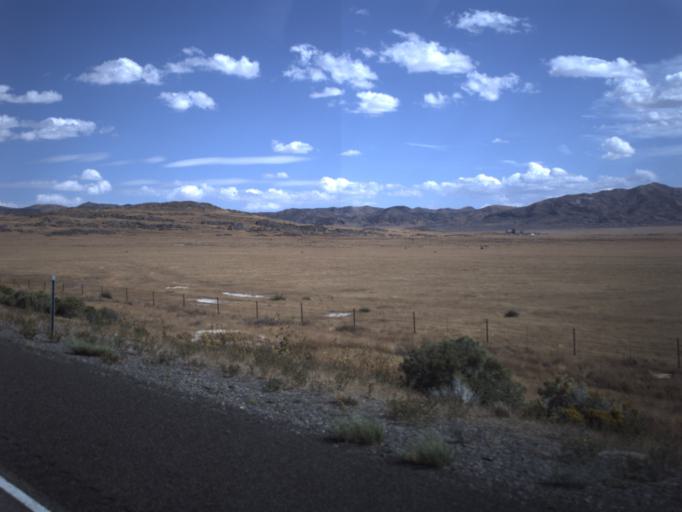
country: US
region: Utah
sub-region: Tooele County
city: Grantsville
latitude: 40.7538
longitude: -113.0326
